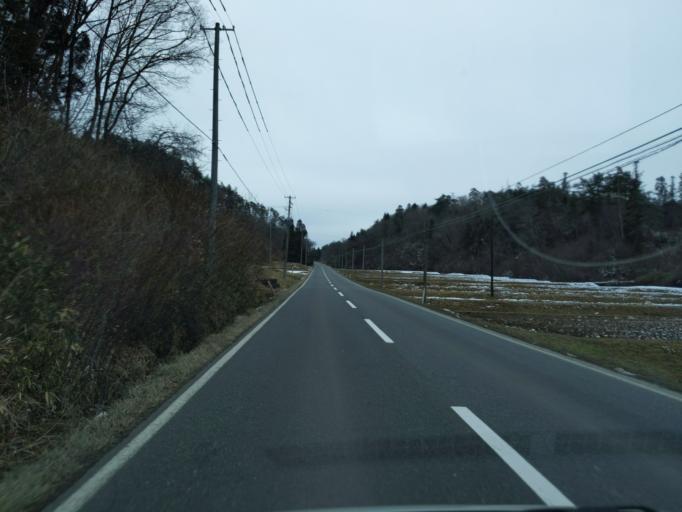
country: JP
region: Iwate
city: Mizusawa
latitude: 39.1493
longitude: 141.2429
